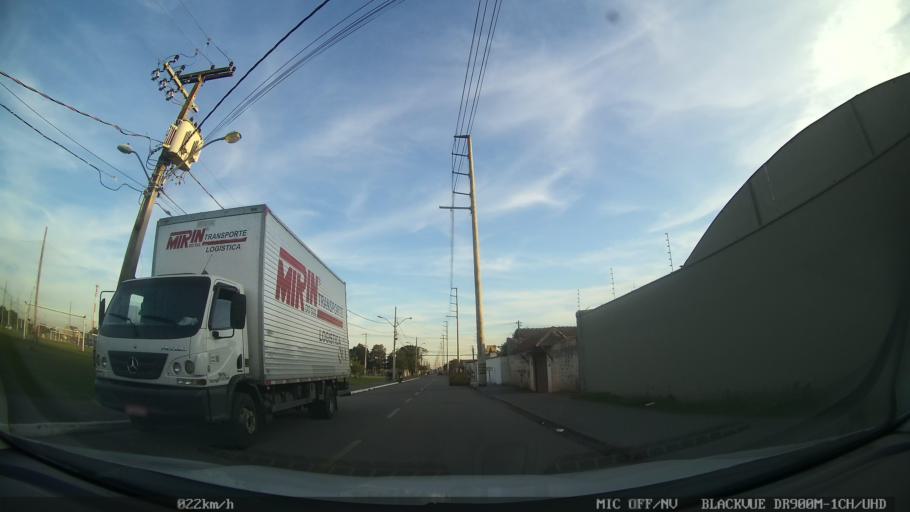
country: BR
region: Parana
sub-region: Pinhais
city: Pinhais
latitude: -25.4444
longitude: -49.1681
